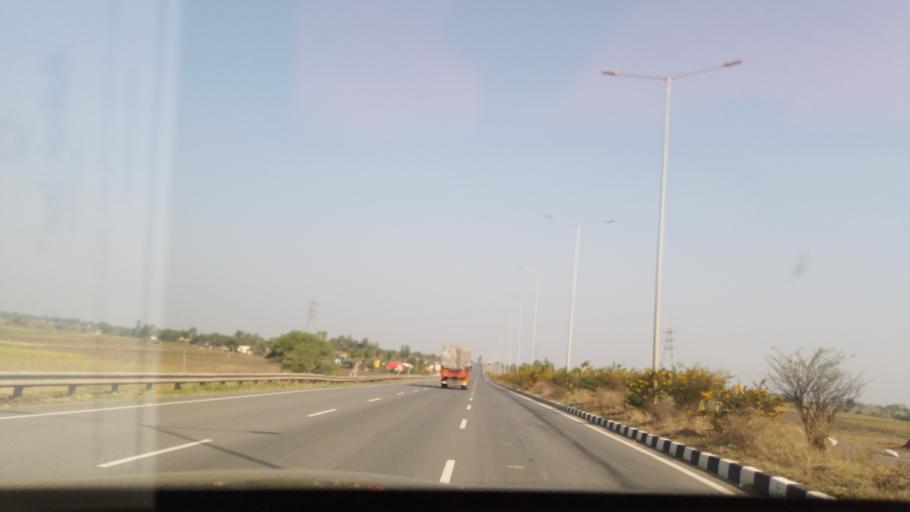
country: IN
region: Karnataka
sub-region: Haveri
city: Savanur
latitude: 14.8649
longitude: 75.3210
